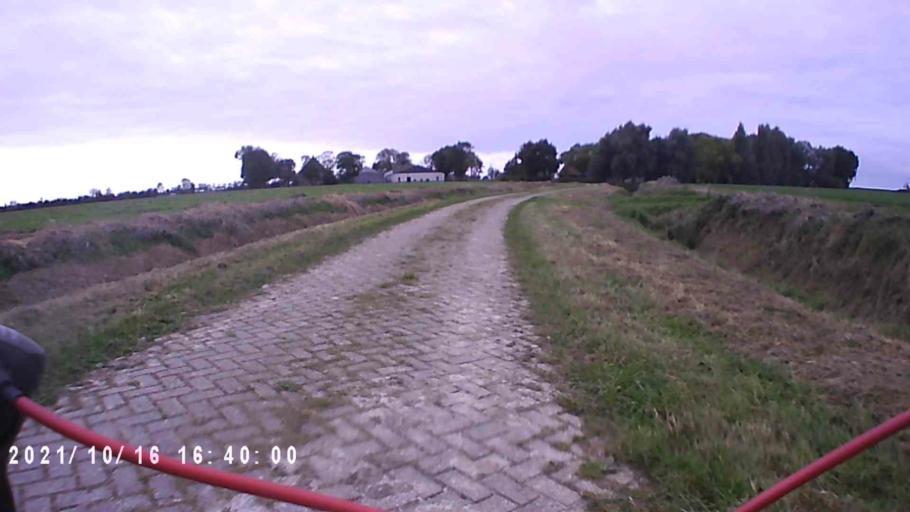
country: NL
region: Friesland
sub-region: Gemeente Dongeradeel
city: Anjum
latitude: 53.3767
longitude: 6.1482
